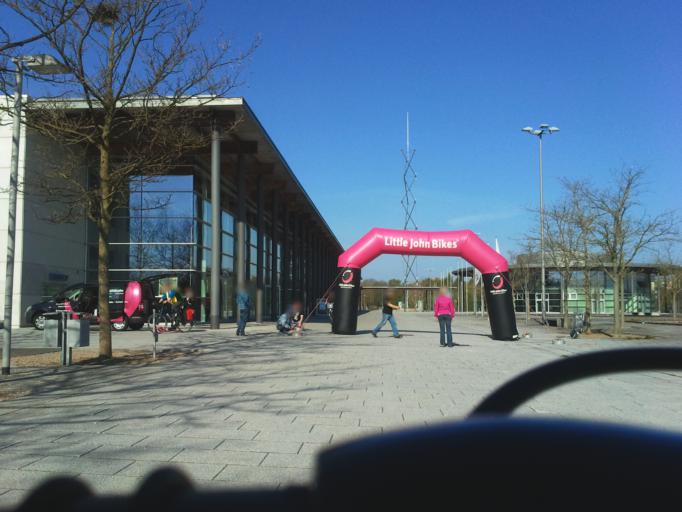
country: DE
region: Mecklenburg-Vorpommern
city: Warnemuende
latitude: 54.1395
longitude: 12.0749
